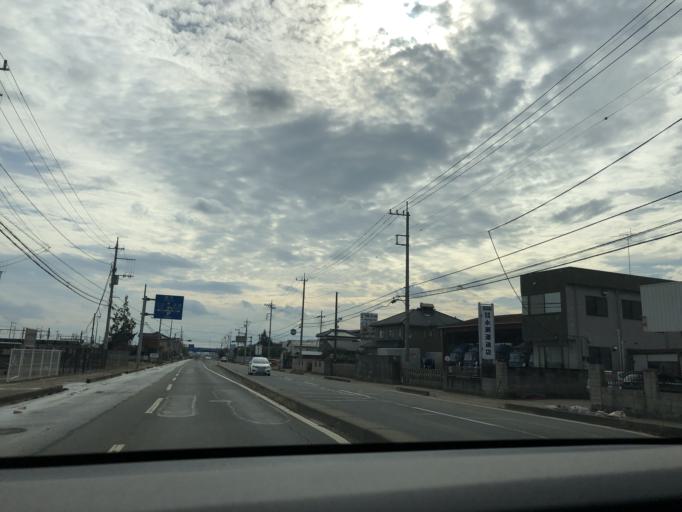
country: JP
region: Tochigi
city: Sano
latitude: 36.2921
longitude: 139.5653
